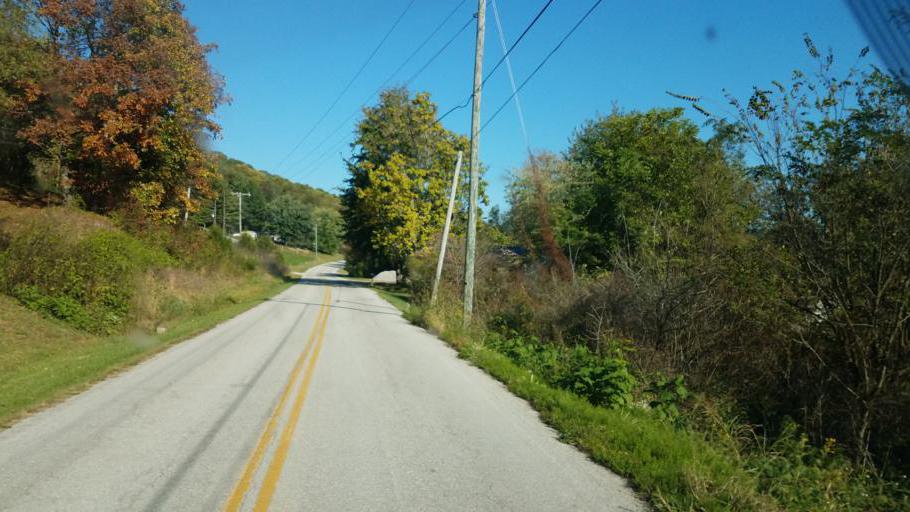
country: US
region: Kentucky
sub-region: Fleming County
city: Flemingsburg
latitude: 38.4670
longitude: -83.5685
